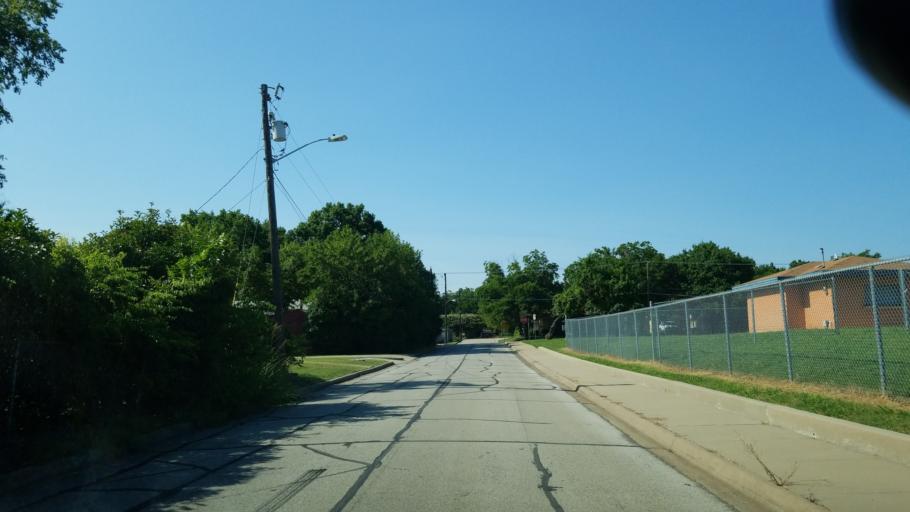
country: US
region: Texas
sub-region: Dallas County
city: Farmers Branch
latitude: 32.9284
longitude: -96.8934
